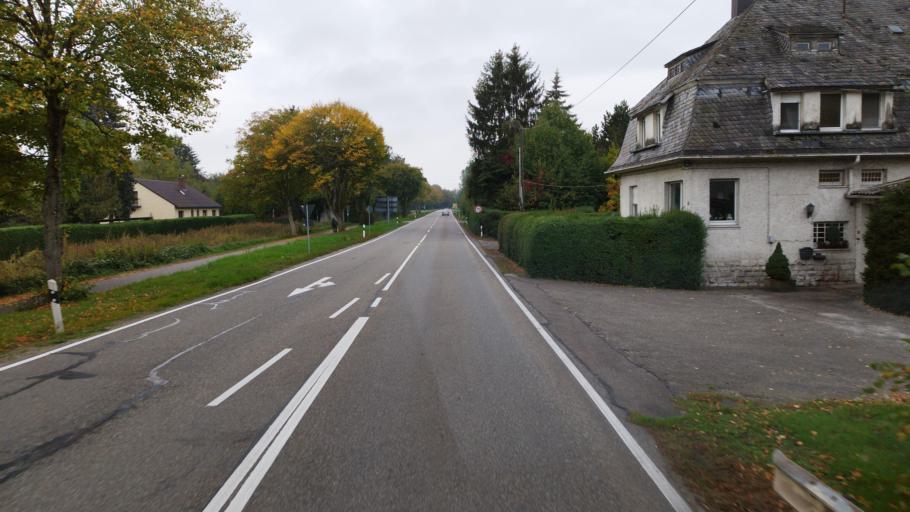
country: DE
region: Baden-Wuerttemberg
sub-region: Karlsruhe Region
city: Rheinau
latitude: 48.8540
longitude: 8.1890
